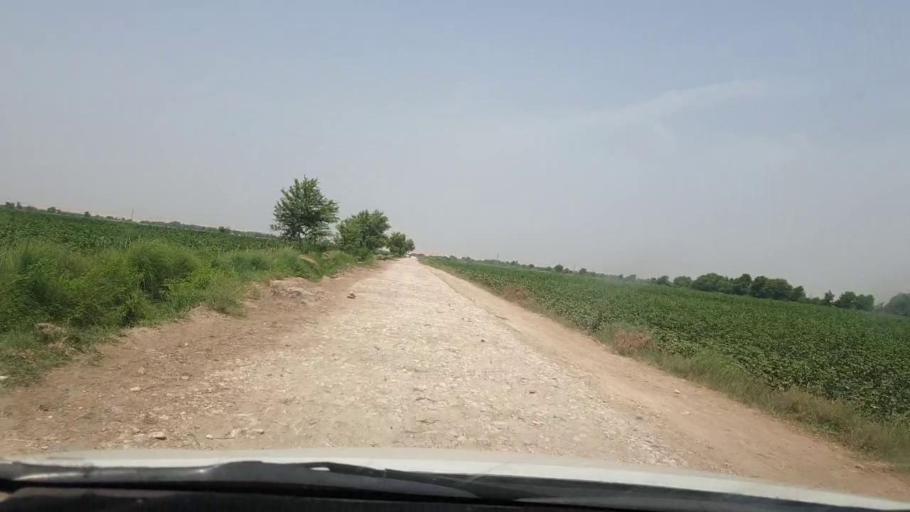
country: PK
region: Sindh
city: Rohri
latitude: 27.4983
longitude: 69.0152
